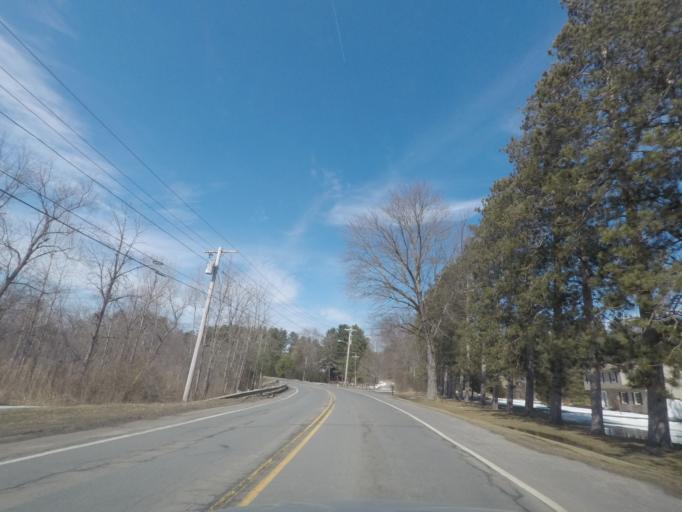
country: US
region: Massachusetts
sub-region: Berkshire County
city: Stockbridge
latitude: 42.2914
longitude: -73.3211
